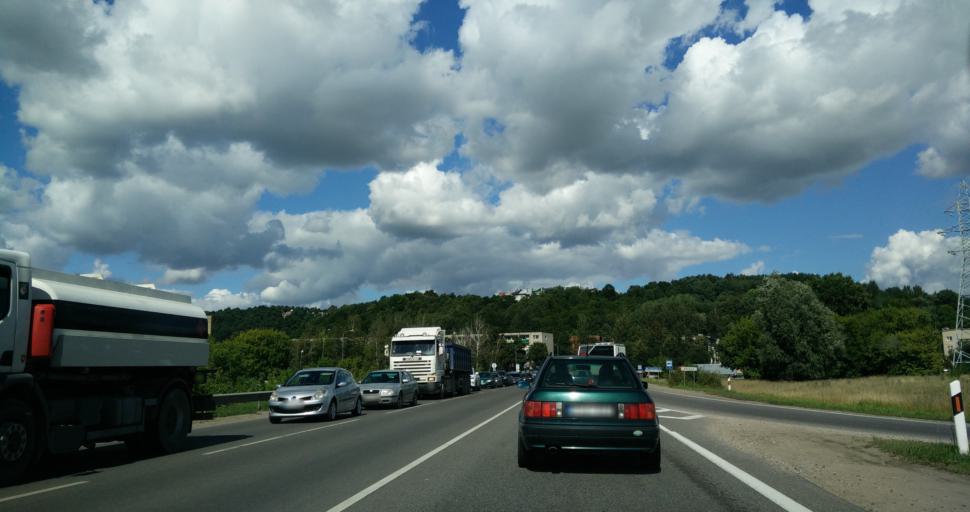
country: LT
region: Kauno apskritis
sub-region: Kauno rajonas
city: Akademija (Kaunas)
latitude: 54.9141
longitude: 23.8342
